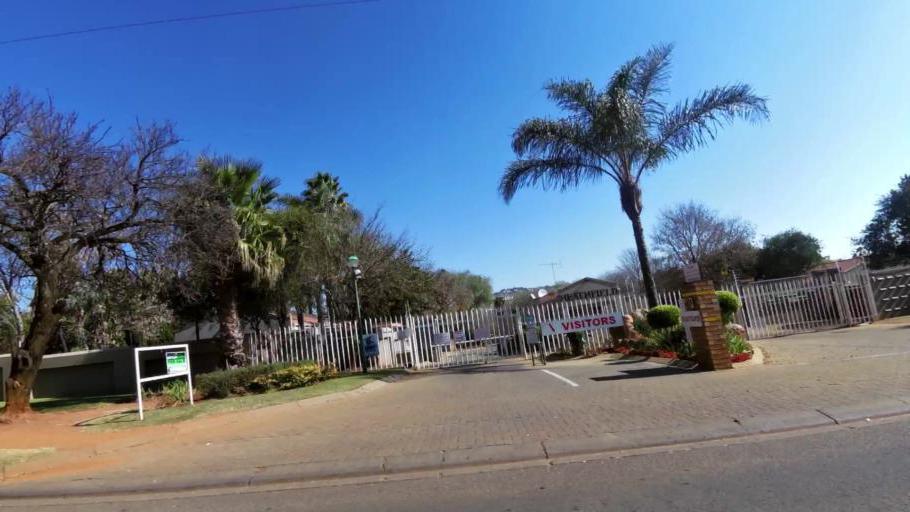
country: ZA
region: Gauteng
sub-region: City of Johannesburg Metropolitan Municipality
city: Roodepoort
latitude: -26.1431
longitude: 27.9362
